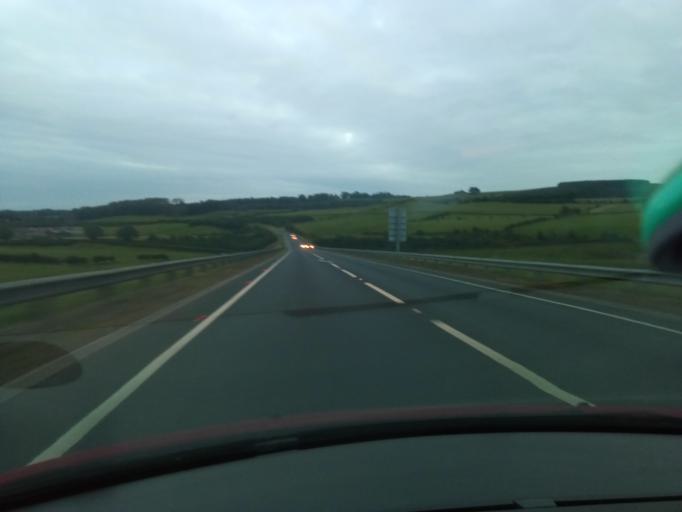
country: GB
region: England
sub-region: Northumberland
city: Bardon Mill
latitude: 54.9673
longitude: -2.2509
